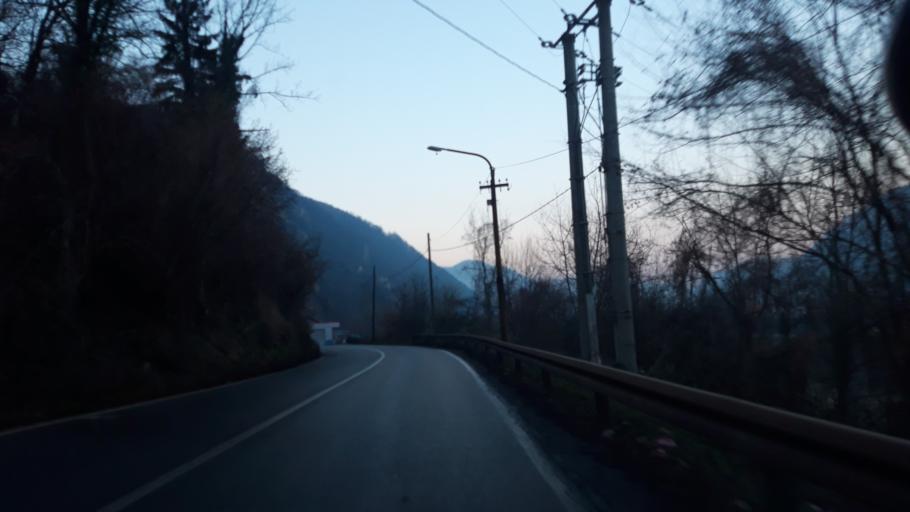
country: RS
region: Central Serbia
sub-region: Macvanski Okrug
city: Mali Zvornik
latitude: 44.3689
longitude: 19.1029
